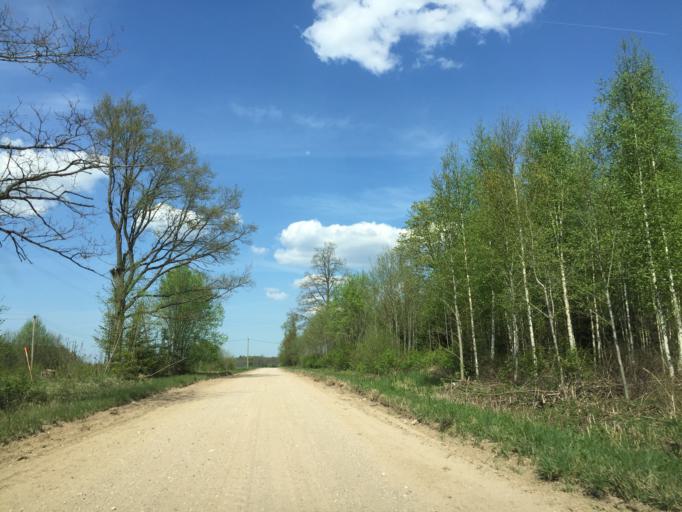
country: LV
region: Limbazu Rajons
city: Limbazi
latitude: 57.3689
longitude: 24.6351
